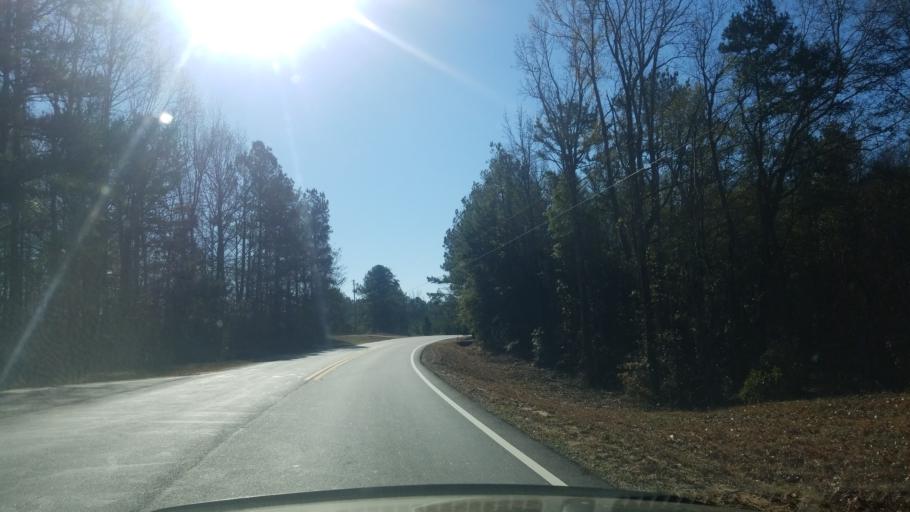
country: US
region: Alabama
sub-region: Chambers County
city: Valley
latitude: 32.8257
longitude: -85.1069
